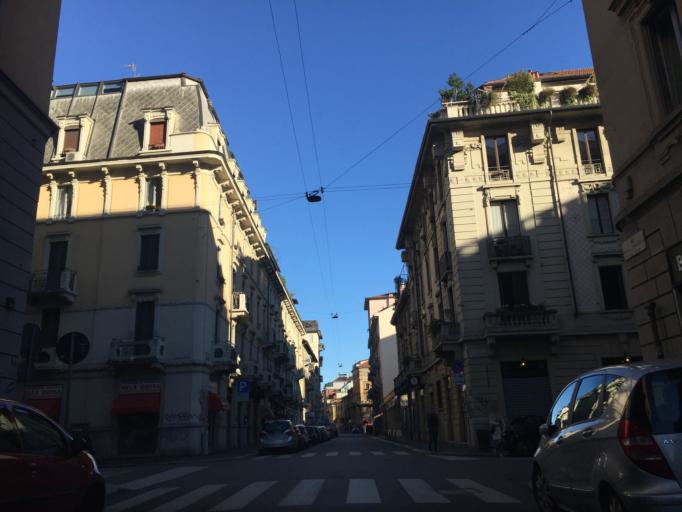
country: IT
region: Lombardy
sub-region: Citta metropolitana di Milano
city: Milano
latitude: 45.4843
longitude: 9.1633
